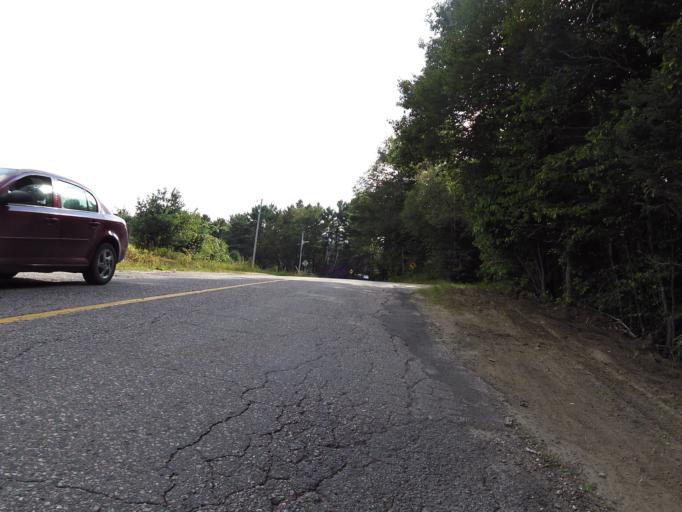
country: CA
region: Quebec
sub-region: Outaouais
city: Wakefield
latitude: 45.6761
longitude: -76.0090
